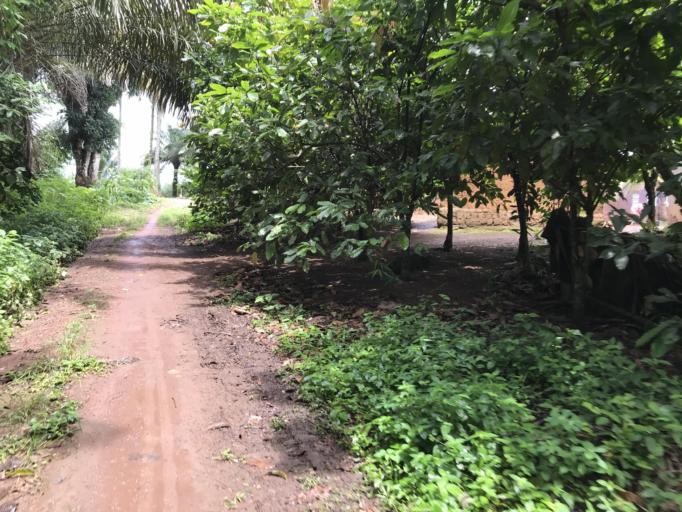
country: SL
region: Eastern Province
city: Buedu
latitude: 8.4706
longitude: -10.3243
